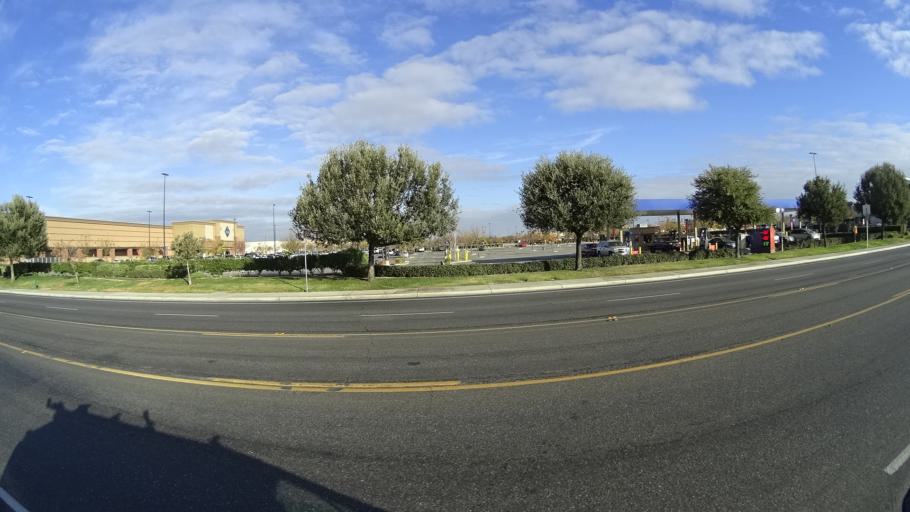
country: US
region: California
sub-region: Kern County
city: Greenacres
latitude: 35.3033
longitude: -119.0942
